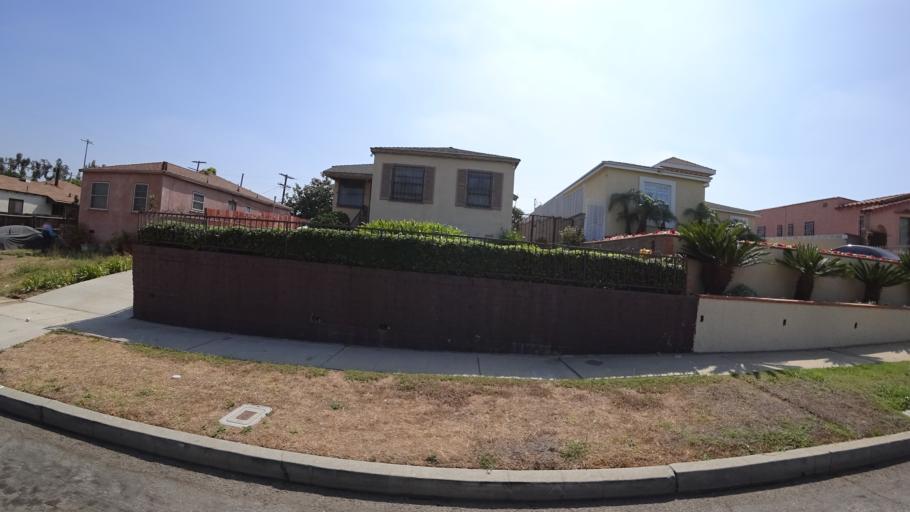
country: US
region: California
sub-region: Los Angeles County
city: Westmont
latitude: 33.9445
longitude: -118.3123
